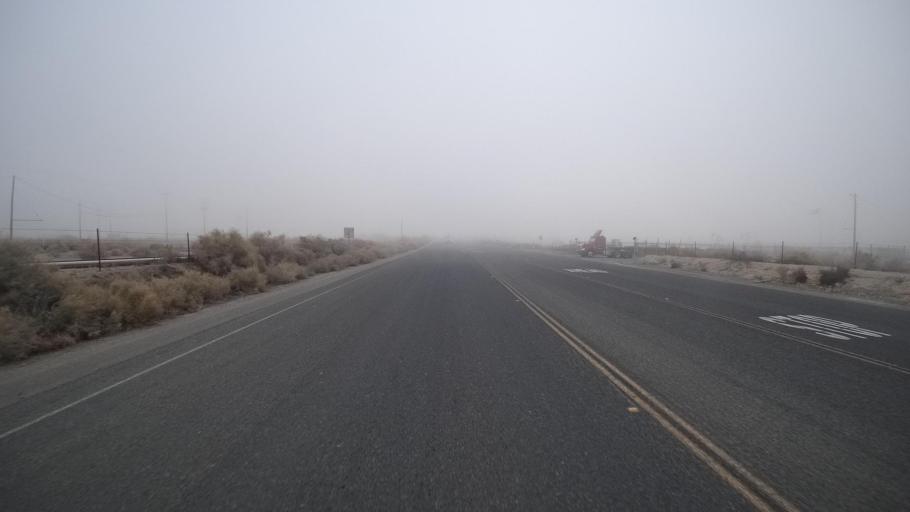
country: US
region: California
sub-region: Kern County
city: Buttonwillow
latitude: 35.2802
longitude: -119.4665
